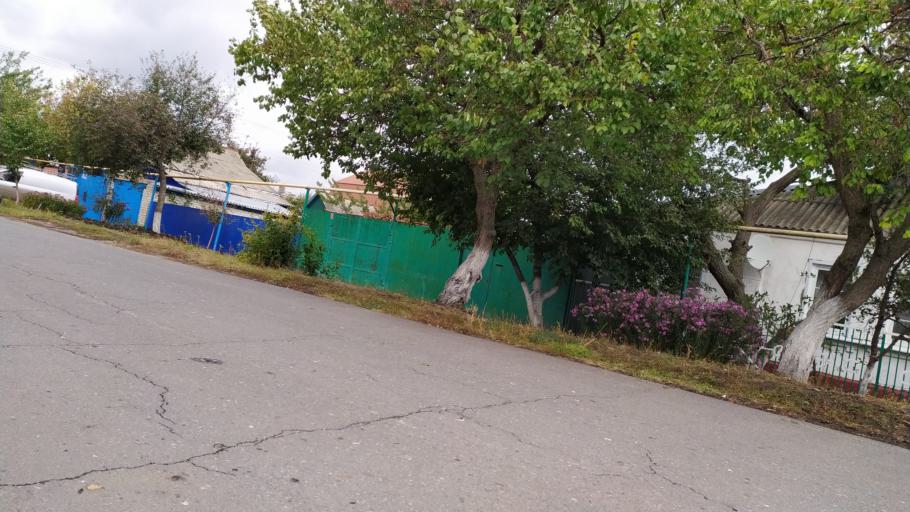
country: RU
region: Kursk
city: Kursk
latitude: 51.6436
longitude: 36.1491
